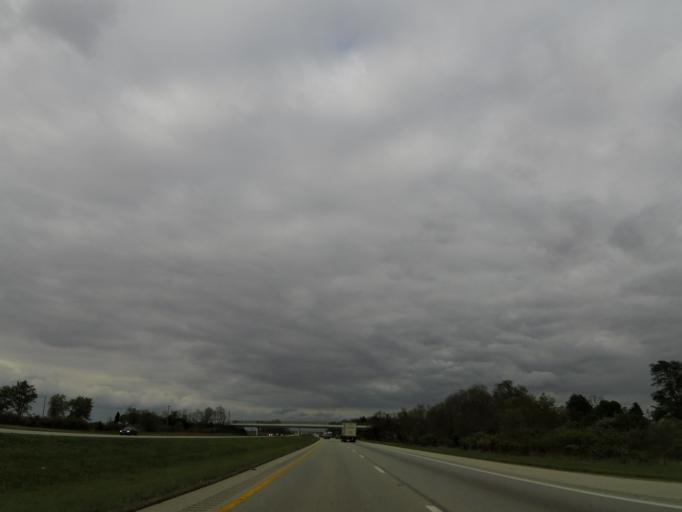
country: US
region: Ohio
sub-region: Clinton County
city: Wilmington
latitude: 39.5340
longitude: -83.7910
